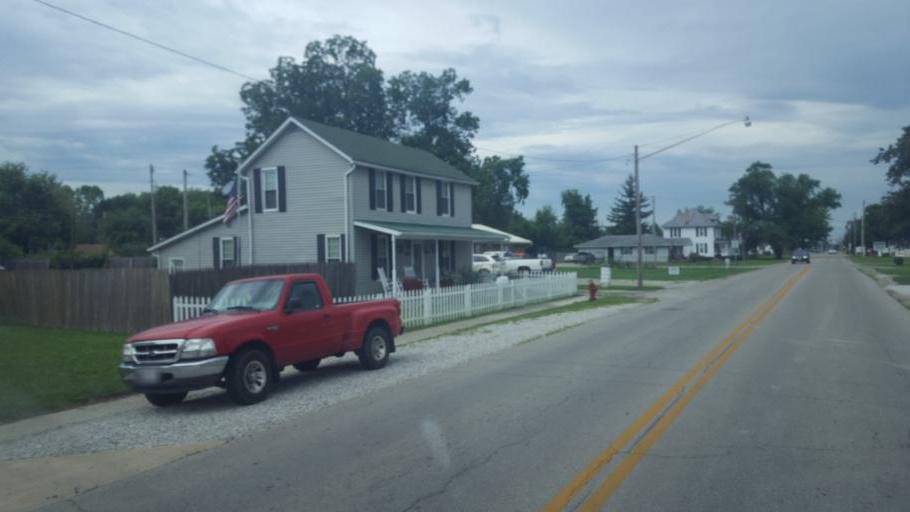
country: US
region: Ohio
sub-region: Pickaway County
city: Ashville
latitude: 39.7199
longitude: -82.9531
